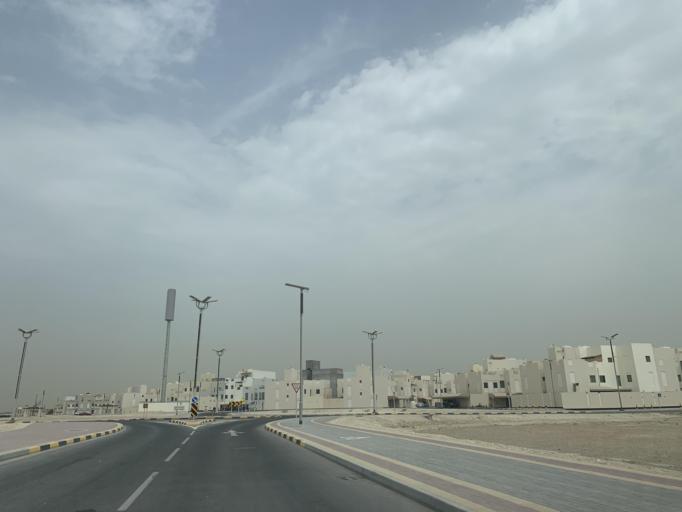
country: BH
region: Northern
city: Madinat `Isa
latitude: 26.1749
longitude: 50.5128
